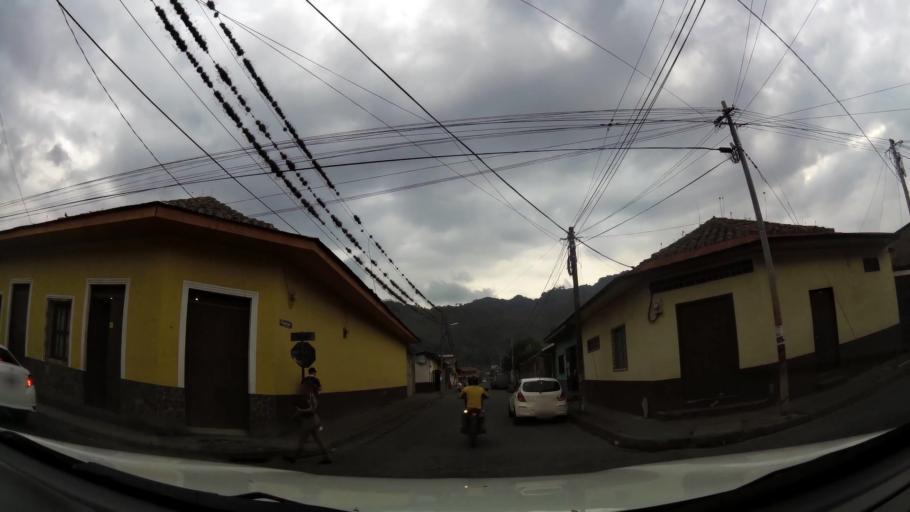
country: NI
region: Jinotega
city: Jinotega
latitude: 13.0879
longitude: -86.0010
